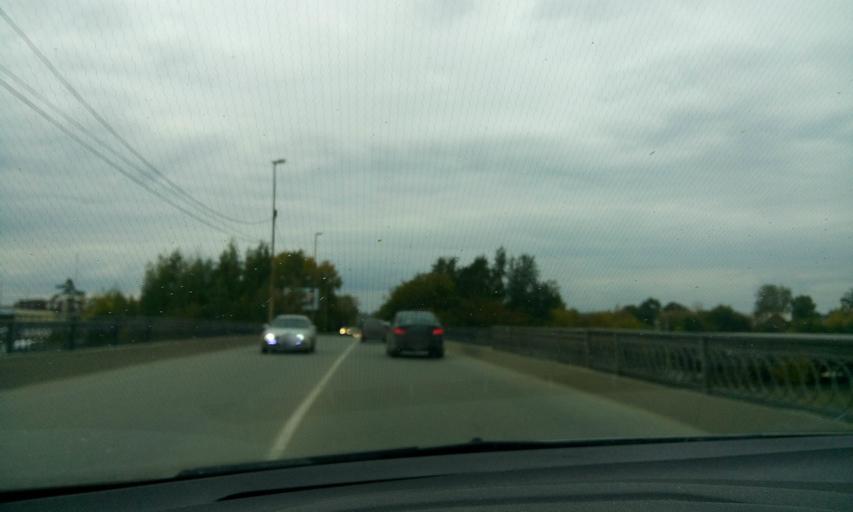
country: RU
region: Sverdlovsk
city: Yekaterinburg
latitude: 56.8675
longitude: 60.6752
